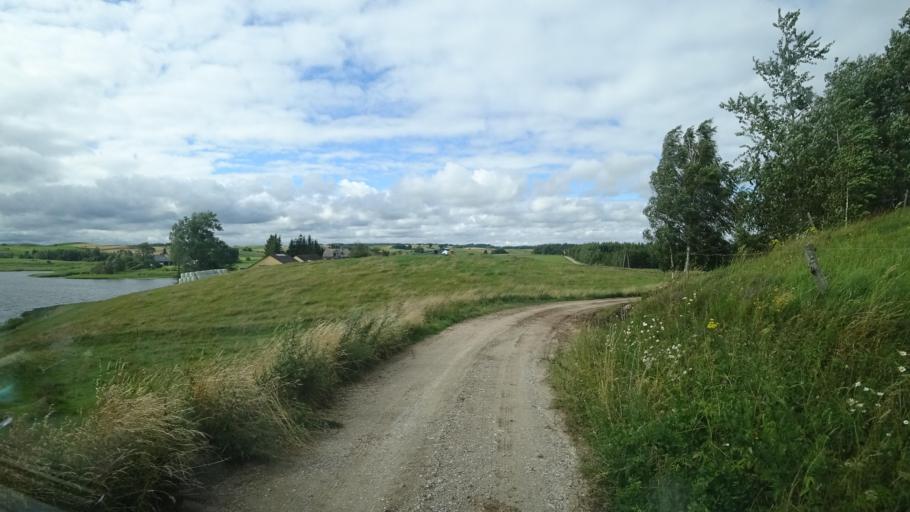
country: PL
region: Podlasie
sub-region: Suwalki
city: Suwalki
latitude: 54.3720
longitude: 22.9005
